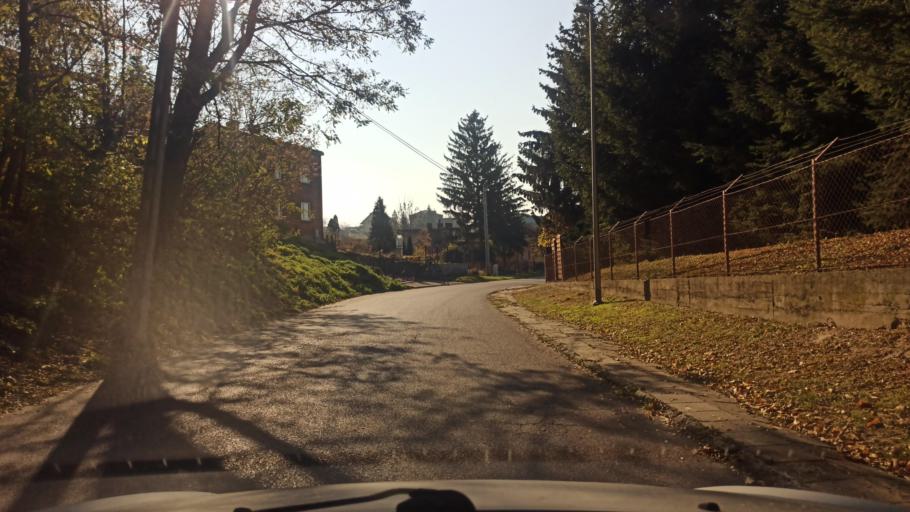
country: PL
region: Subcarpathian Voivodeship
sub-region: Powiat jaroslawski
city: Radymno
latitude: 49.9457
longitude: 22.8223
